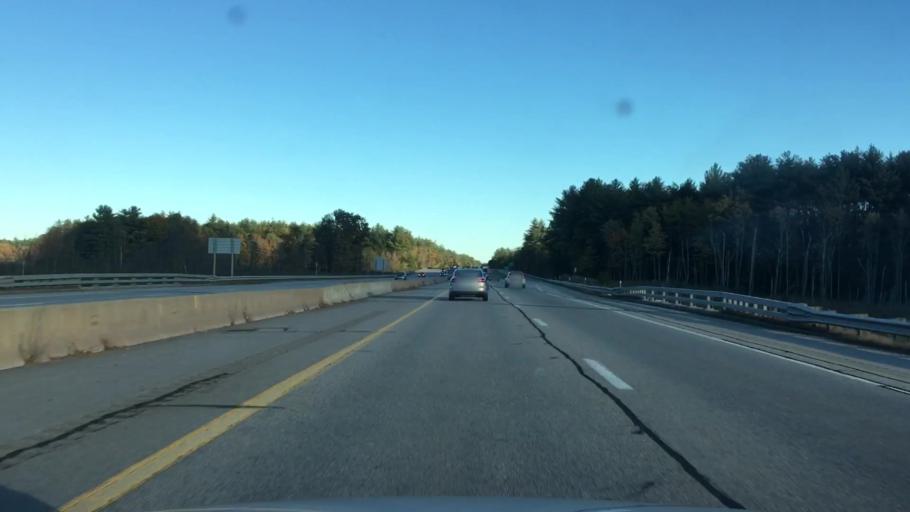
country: US
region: New Hampshire
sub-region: Rockingham County
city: Epping
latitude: 43.0245
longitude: -71.0633
